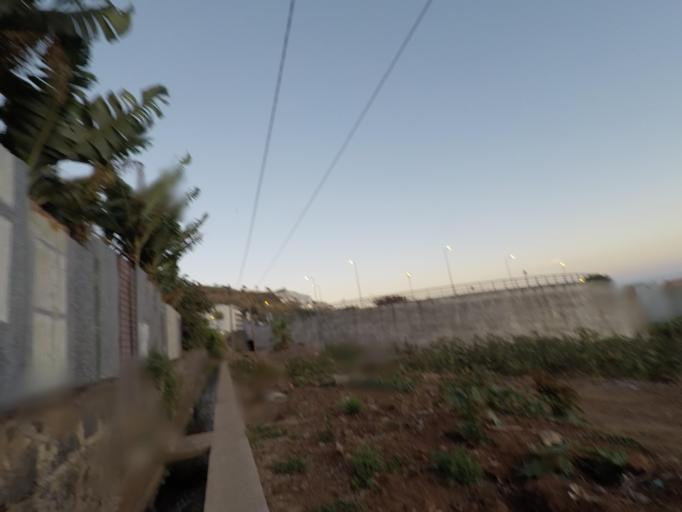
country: PT
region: Madeira
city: Camara de Lobos
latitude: 32.6459
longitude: -16.9461
